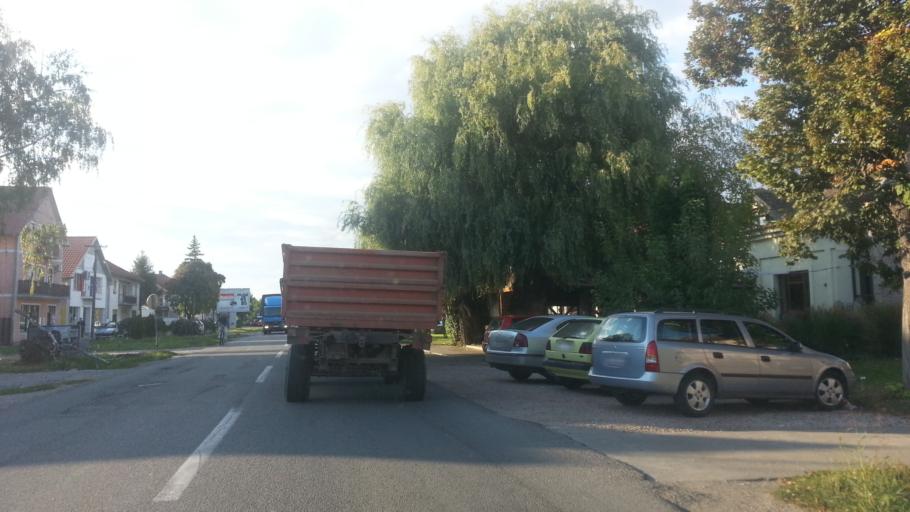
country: RS
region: Autonomna Pokrajina Vojvodina
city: Nova Pazova
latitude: 44.9456
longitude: 20.2174
